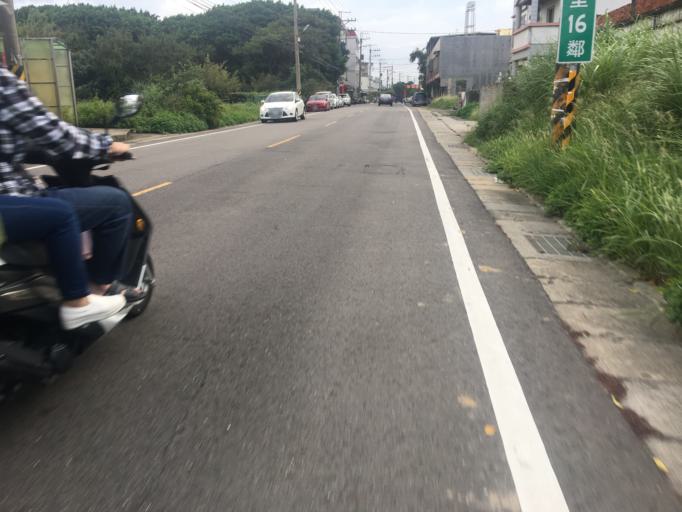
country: TW
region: Taiwan
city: Taoyuan City
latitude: 25.0963
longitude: 121.2355
